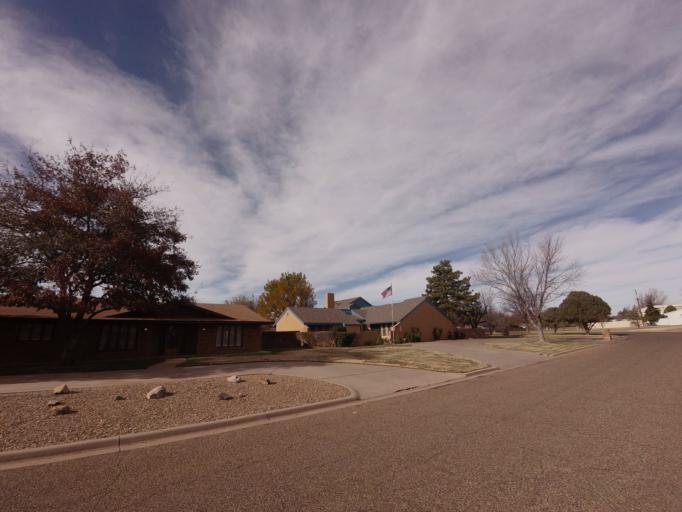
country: US
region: New Mexico
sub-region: Curry County
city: Clovis
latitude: 34.4177
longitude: -103.1848
